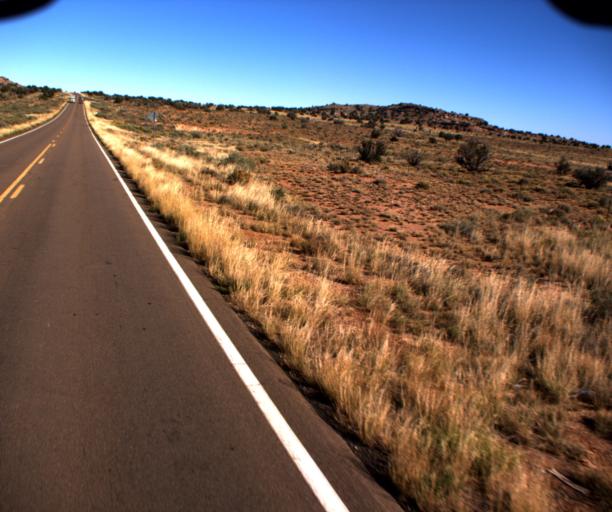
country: US
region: Arizona
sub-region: Navajo County
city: Snowflake
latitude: 34.6808
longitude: -110.1039
